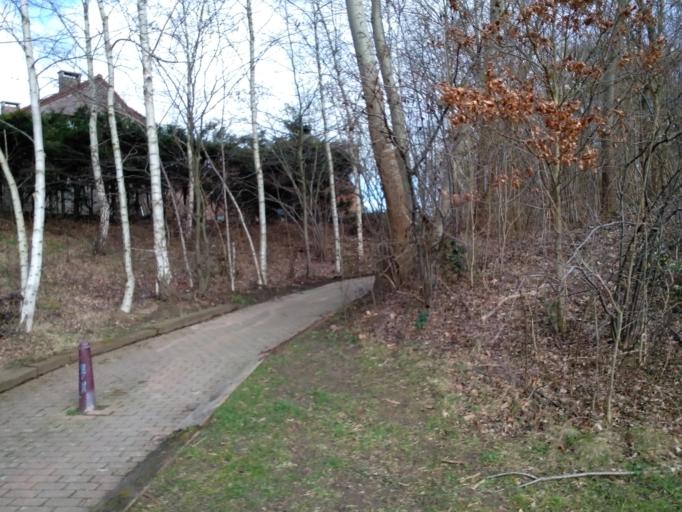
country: BE
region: Flanders
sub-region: Provincie Vlaams-Brabant
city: Leuven
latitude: 50.8672
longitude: 4.6713
